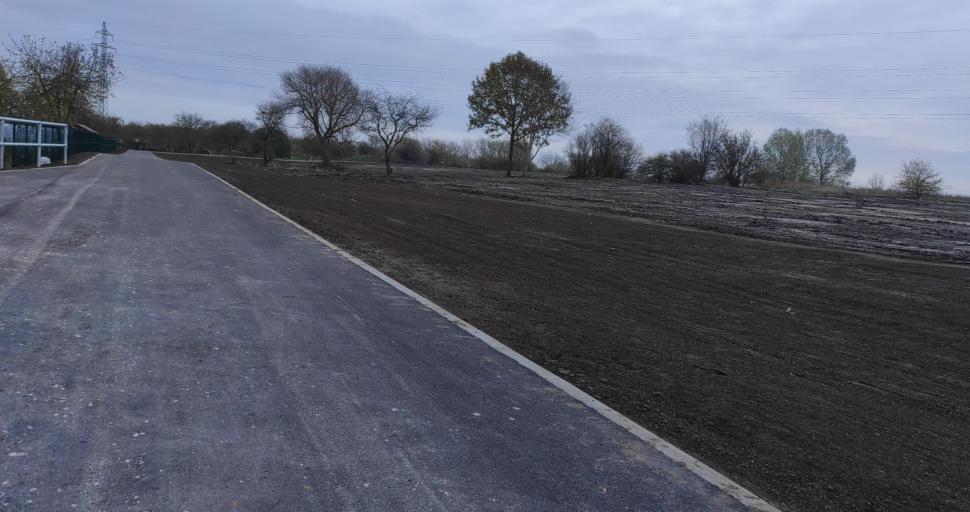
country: LV
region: Liepaja
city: Liepaja
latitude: 56.5173
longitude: 21.0348
